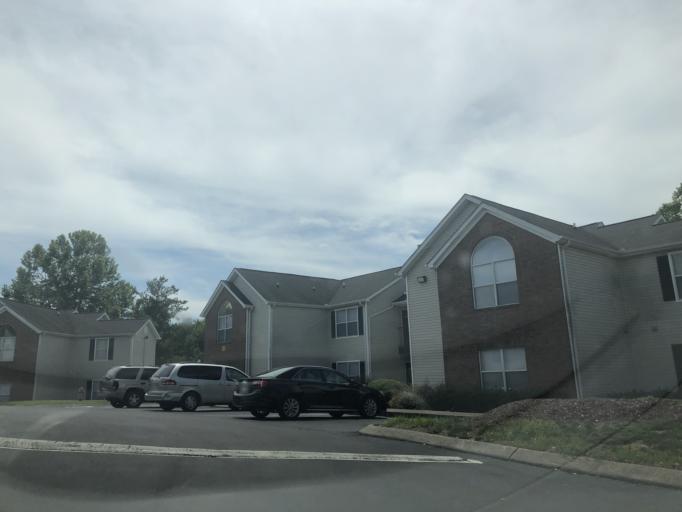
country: US
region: Tennessee
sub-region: Davidson County
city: Belle Meade
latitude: 36.0760
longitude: -86.9286
